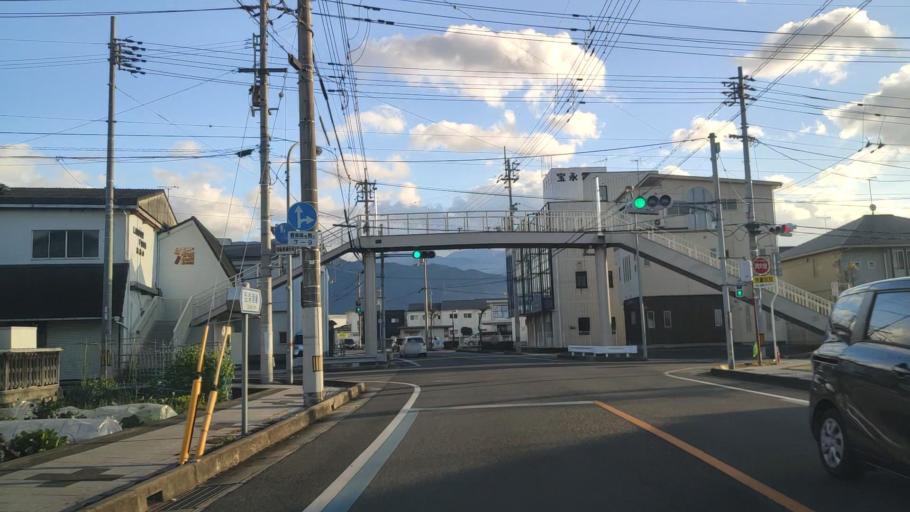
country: JP
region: Ehime
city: Saijo
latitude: 33.9148
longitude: 133.1779
